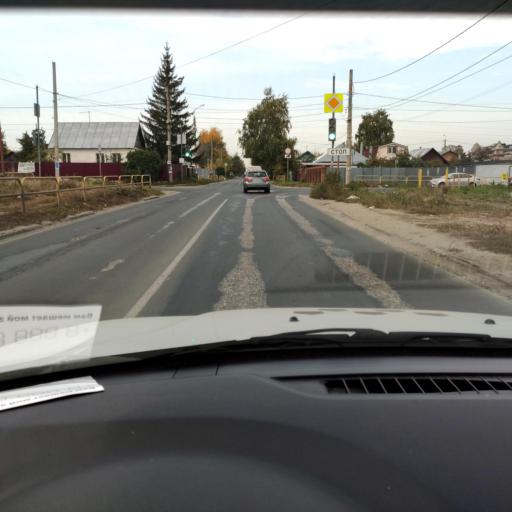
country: RU
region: Samara
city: Tol'yatti
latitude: 53.5351
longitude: 49.4294
